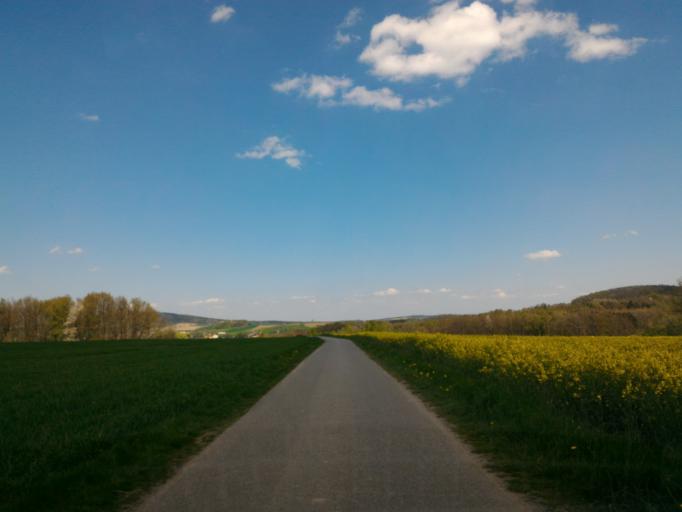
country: DE
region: Saxony
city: Leutersdorf
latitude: 50.9548
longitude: 14.6695
